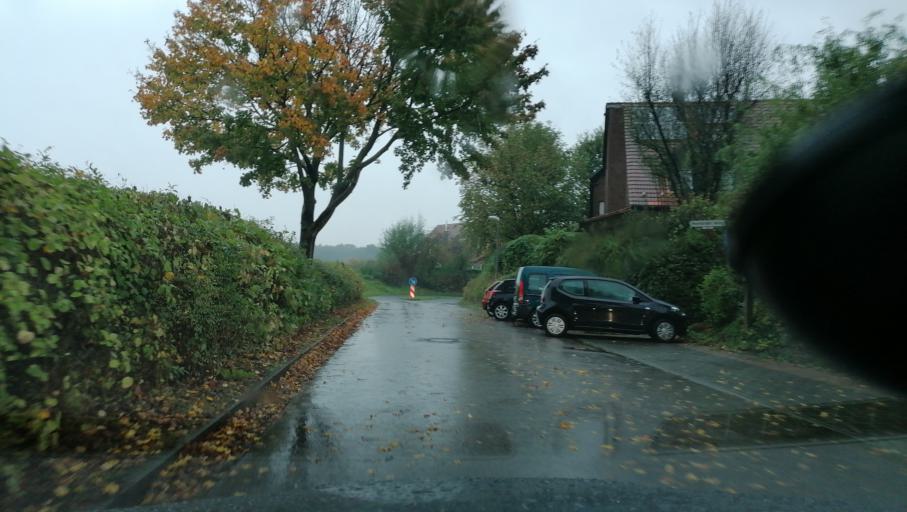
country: DE
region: North Rhine-Westphalia
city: Herten
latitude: 51.5904
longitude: 7.1733
